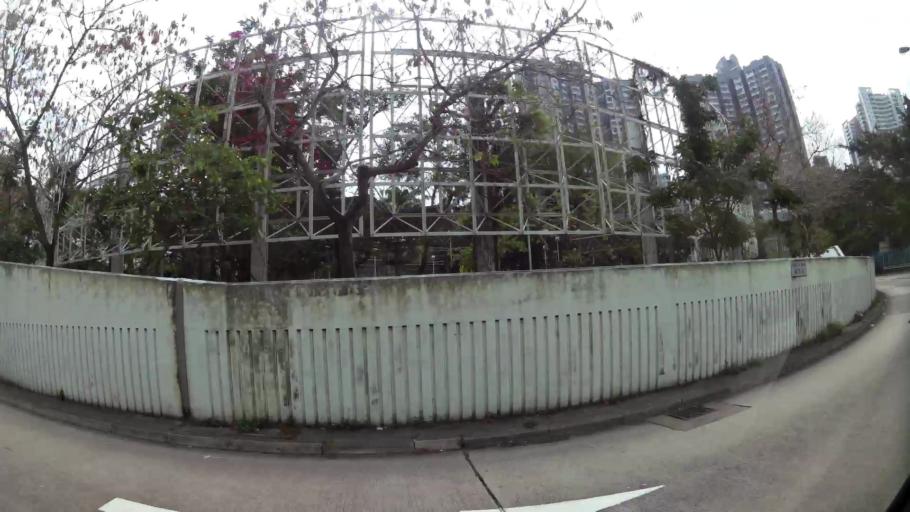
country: HK
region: Wanchai
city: Wan Chai
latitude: 22.2691
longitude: 114.2384
